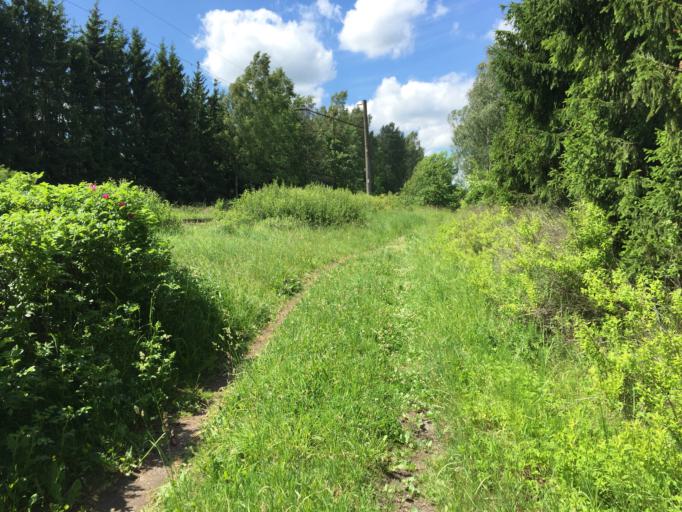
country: LV
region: Engure
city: Smarde
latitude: 56.9574
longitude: 23.3303
